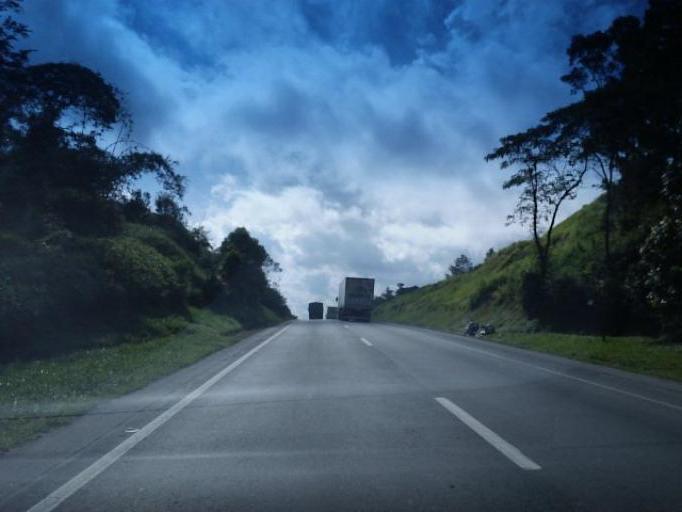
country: BR
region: Parana
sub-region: Antonina
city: Antonina
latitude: -25.1083
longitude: -48.7721
